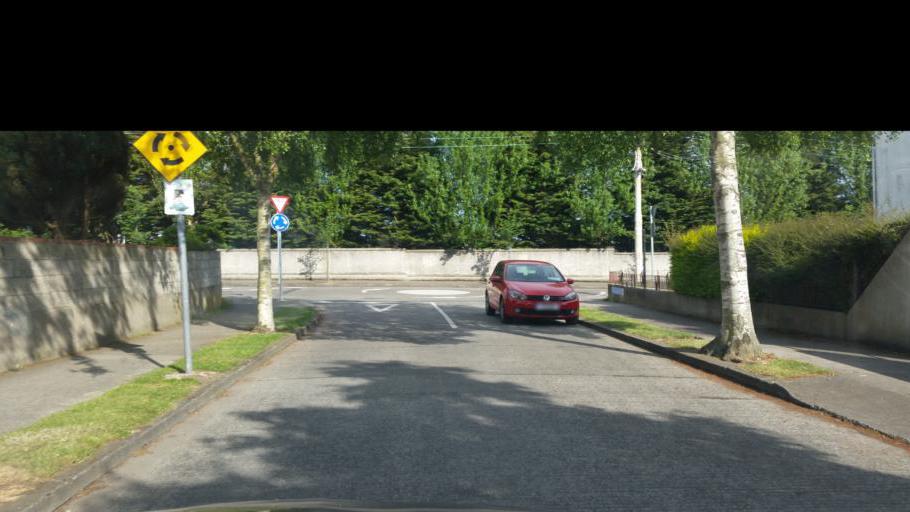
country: IE
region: Leinster
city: Cabra
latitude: 53.3641
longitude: -6.2997
